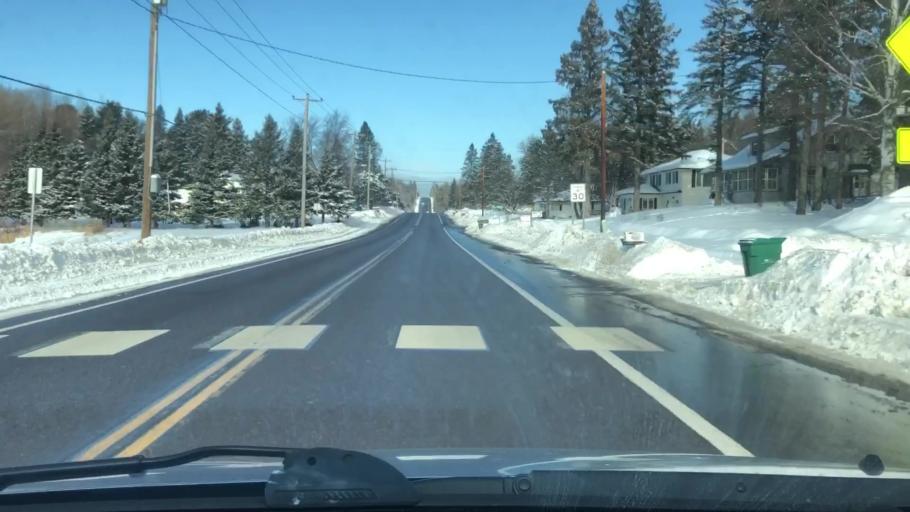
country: US
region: Minnesota
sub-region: Saint Louis County
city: Duluth
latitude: 46.8040
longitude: -92.1322
